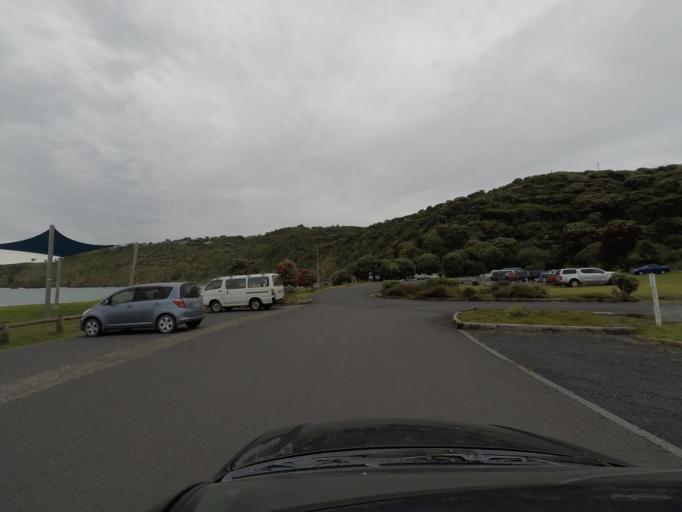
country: NZ
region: Waikato
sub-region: Waikato District
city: Raglan
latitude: -37.8216
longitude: 174.8132
